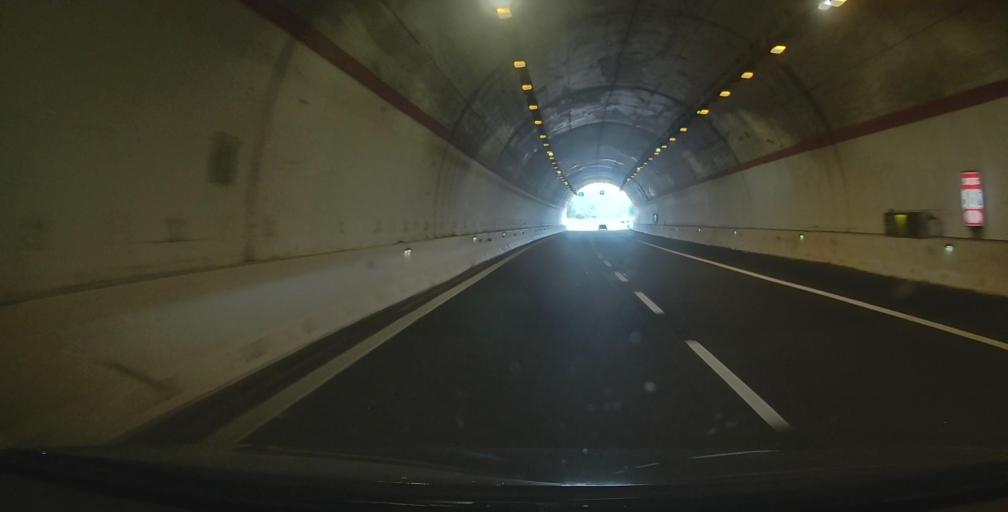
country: IT
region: Calabria
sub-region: Provincia di Vibo-Valentia
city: Filogaso
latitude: 38.6524
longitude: 16.1882
